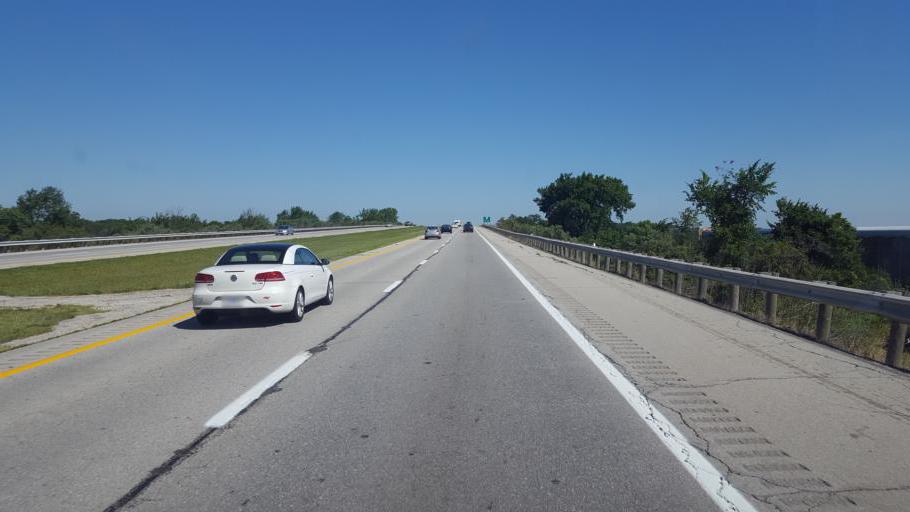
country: US
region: Ohio
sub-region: Marion County
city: Marion
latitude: 40.6452
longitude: -83.0997
